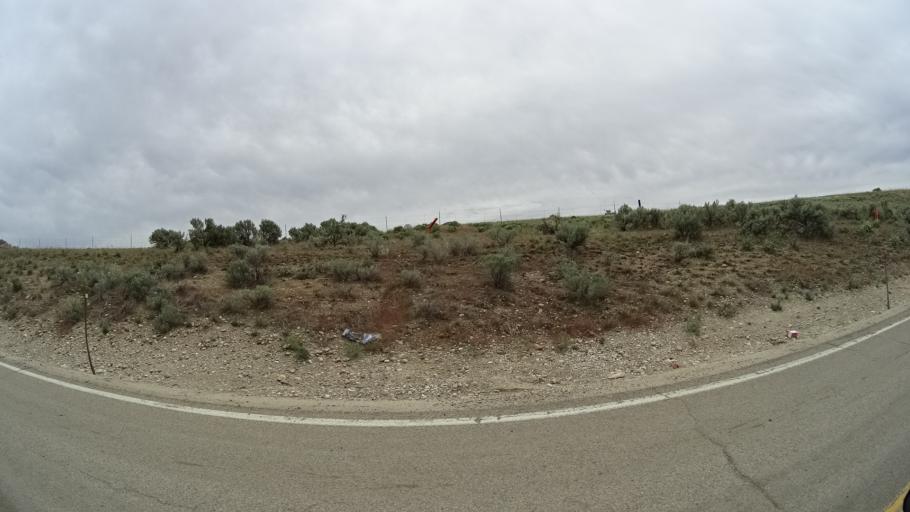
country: US
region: Idaho
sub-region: Ada County
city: Boise
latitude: 43.4641
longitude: -116.0914
